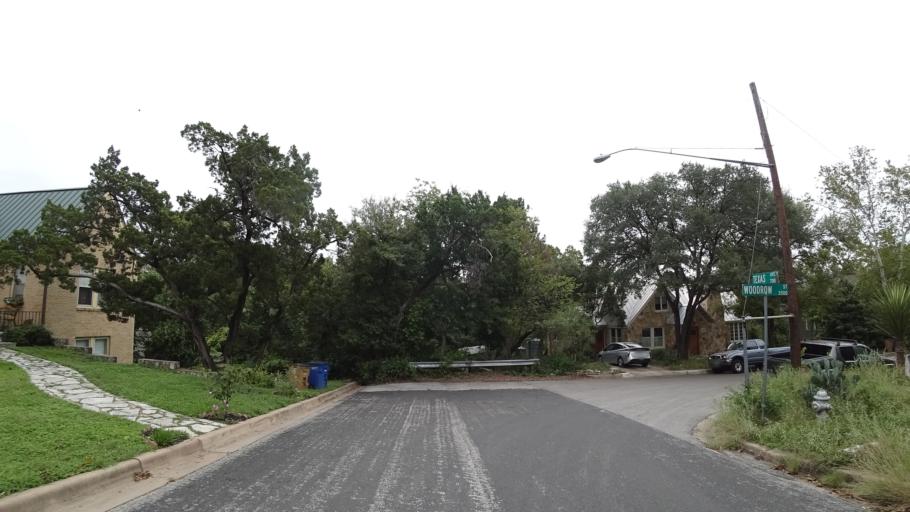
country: US
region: Texas
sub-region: Travis County
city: Austin
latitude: 30.2966
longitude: -97.7279
